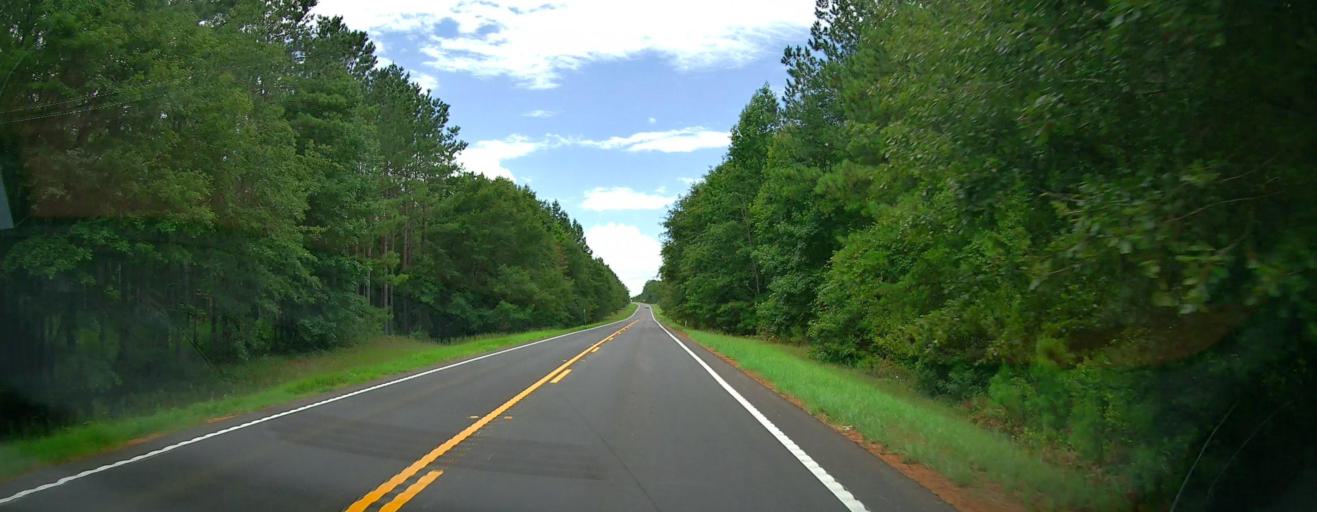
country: US
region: Georgia
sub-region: Dooly County
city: Vienna
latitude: 32.0794
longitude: -83.6114
